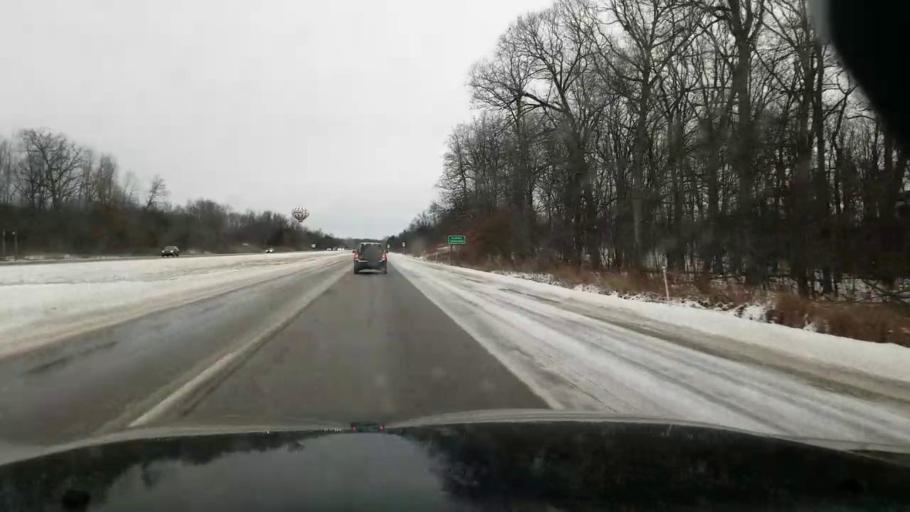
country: US
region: Michigan
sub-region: Jackson County
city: Jackson
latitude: 42.2476
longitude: -84.4761
